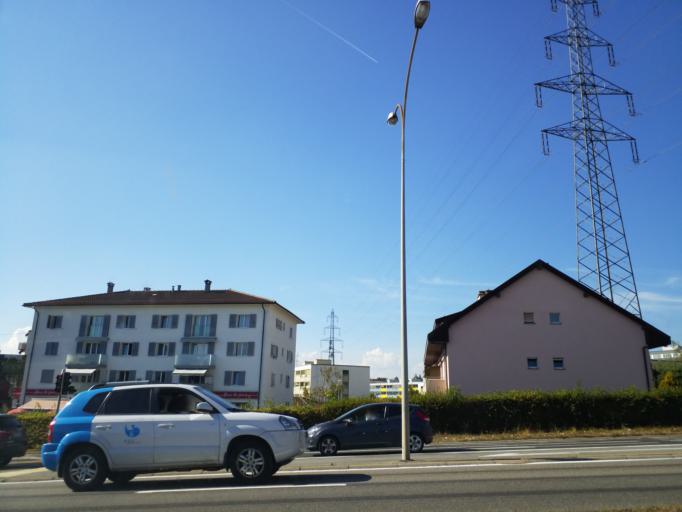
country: CH
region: Vaud
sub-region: Lausanne District
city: Epalinges
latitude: 46.5437
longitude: 6.6618
